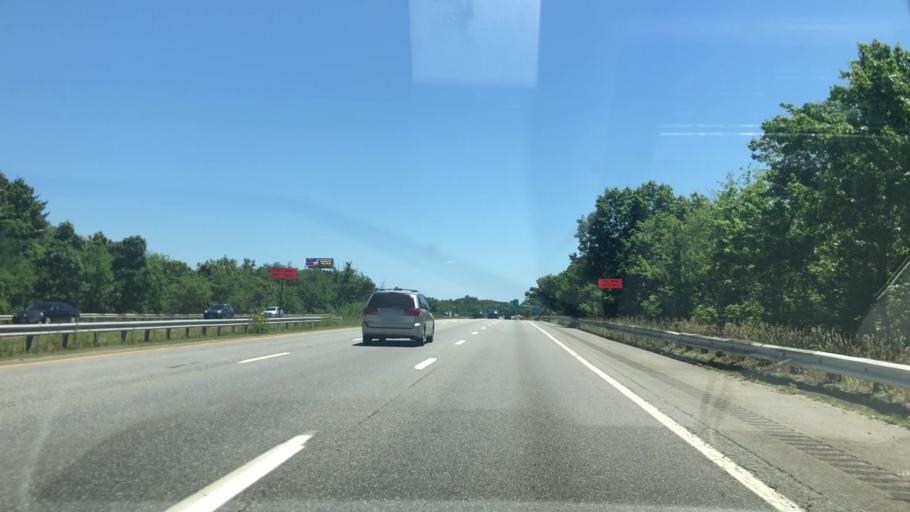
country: US
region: Massachusetts
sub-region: Essex County
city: Methuen
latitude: 42.7455
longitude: -71.2121
